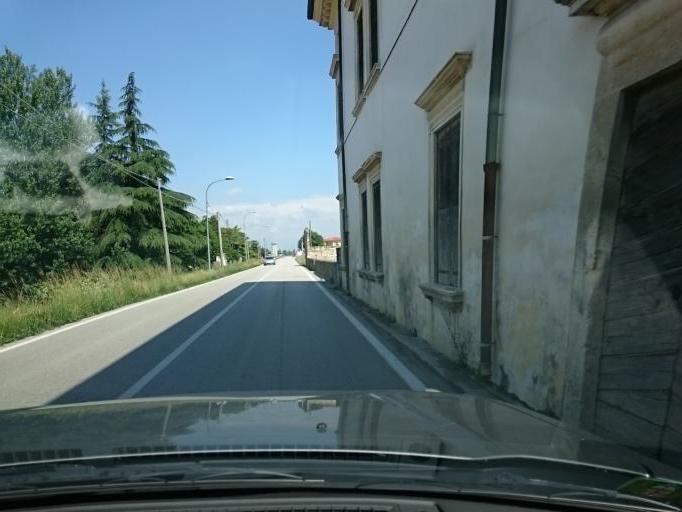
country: IT
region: Veneto
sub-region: Provincia di Vicenza
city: Longare
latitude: 45.4697
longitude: 11.6267
